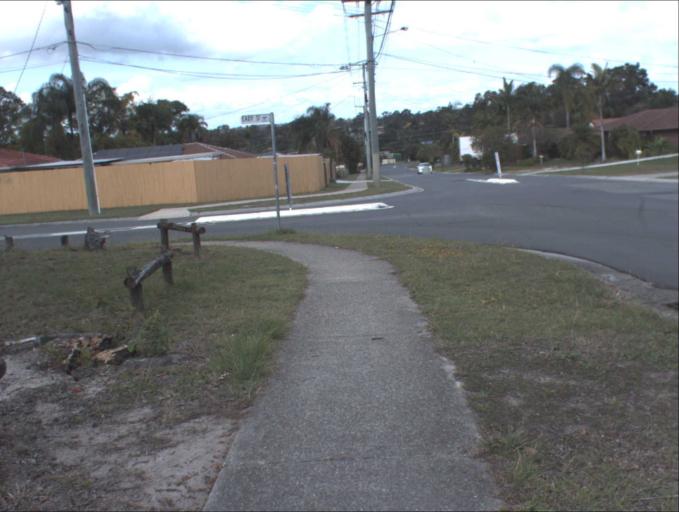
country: AU
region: Queensland
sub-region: Brisbane
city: Sunnybank Hills
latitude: -27.6597
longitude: 153.0569
